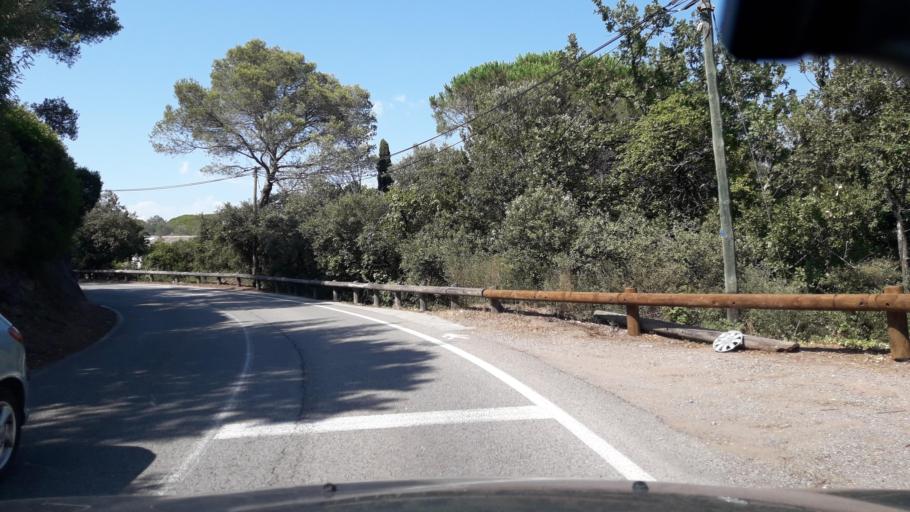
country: FR
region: Provence-Alpes-Cote d'Azur
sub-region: Departement du Var
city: Saint-Raphael
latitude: 43.4497
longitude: 6.7619
